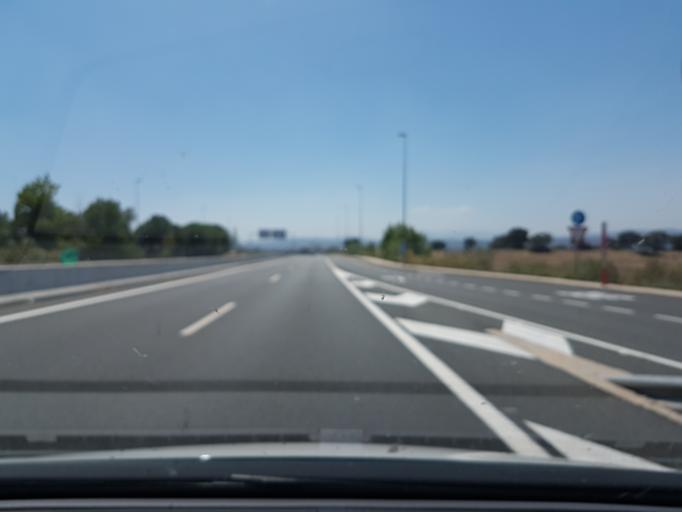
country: ES
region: Madrid
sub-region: Provincia de Madrid
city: Villanueva de Perales
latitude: 40.3816
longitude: -4.0837
